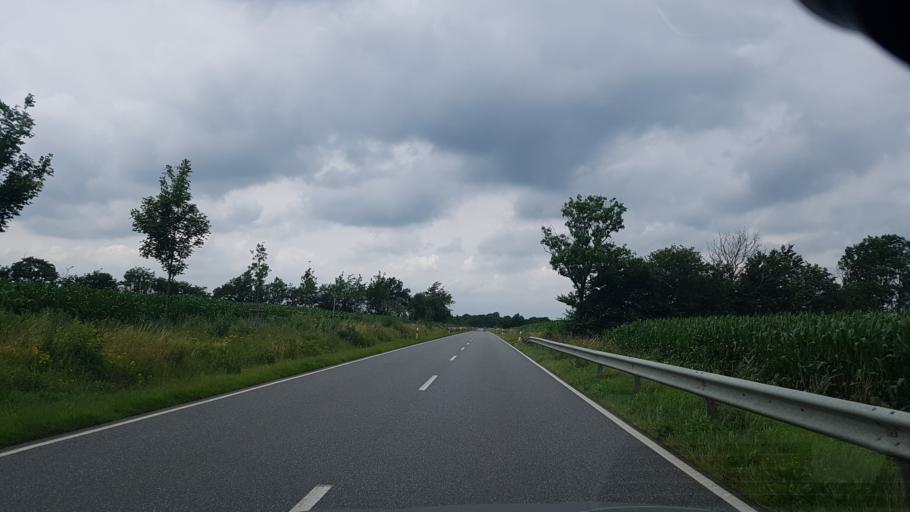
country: DE
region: Schleswig-Holstein
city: Boxlund
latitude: 54.8533
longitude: 9.1841
